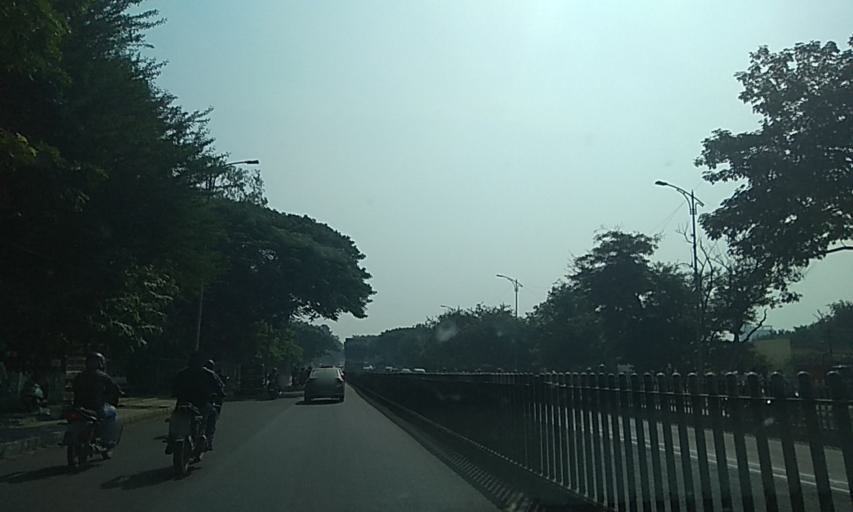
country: IN
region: Maharashtra
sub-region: Pune Division
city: Shivaji Nagar
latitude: 18.5464
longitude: 73.8748
